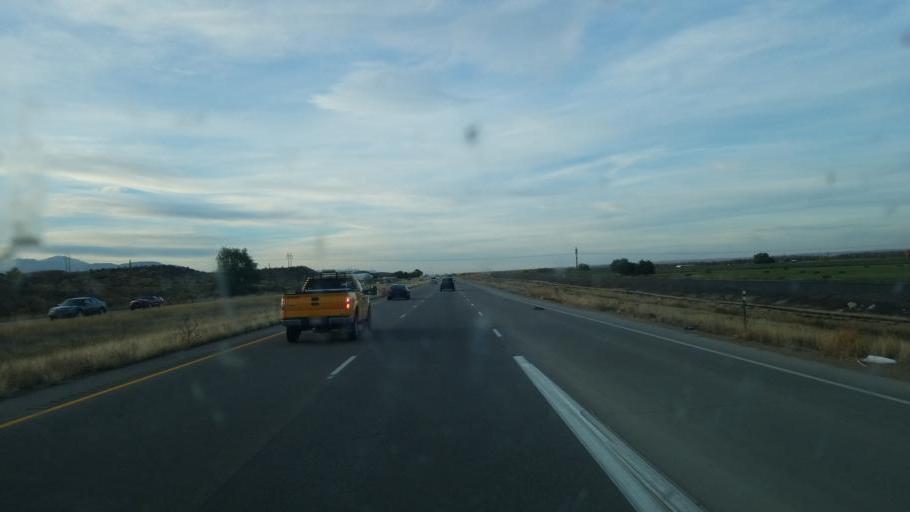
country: US
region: Colorado
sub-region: El Paso County
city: Fountain
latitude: 38.5549
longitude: -104.6486
